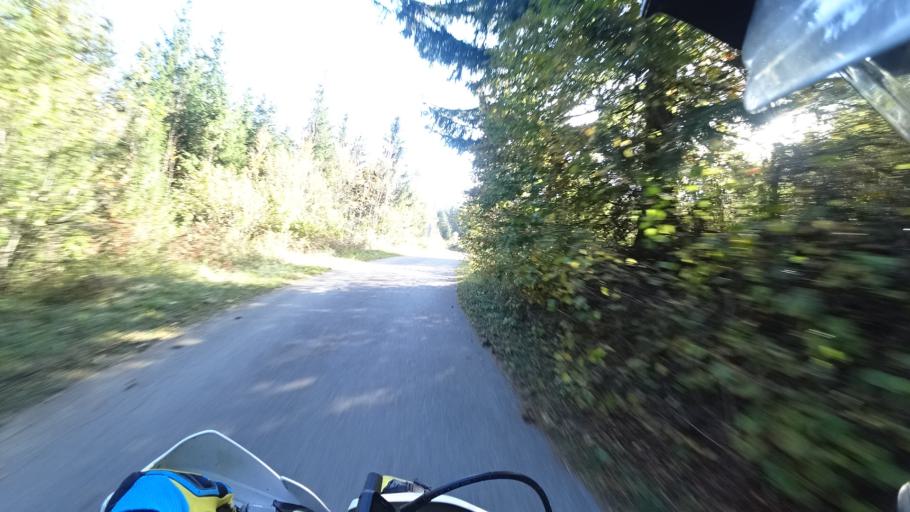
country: HR
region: Karlovacka
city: Plaski
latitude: 44.9858
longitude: 15.4172
